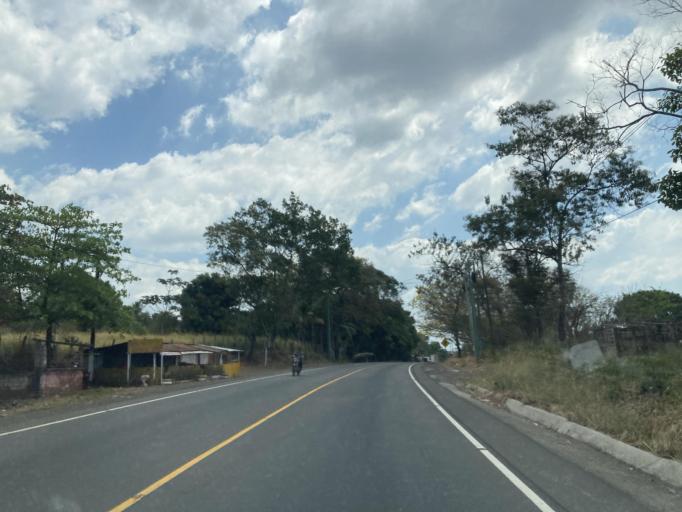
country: GT
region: Santa Rosa
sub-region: Municipio de Taxisco
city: Taxisco
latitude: 14.0893
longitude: -90.4983
